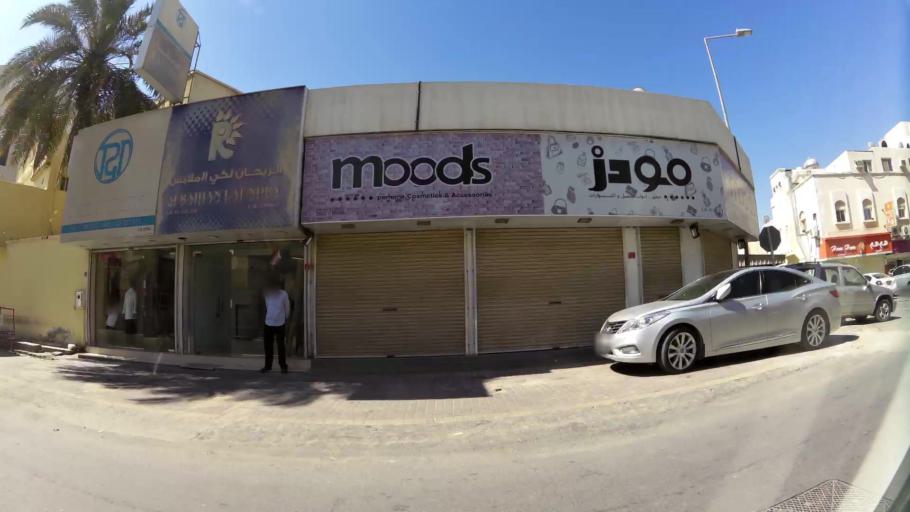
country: BH
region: Muharraq
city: Al Muharraq
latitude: 26.2618
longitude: 50.6177
